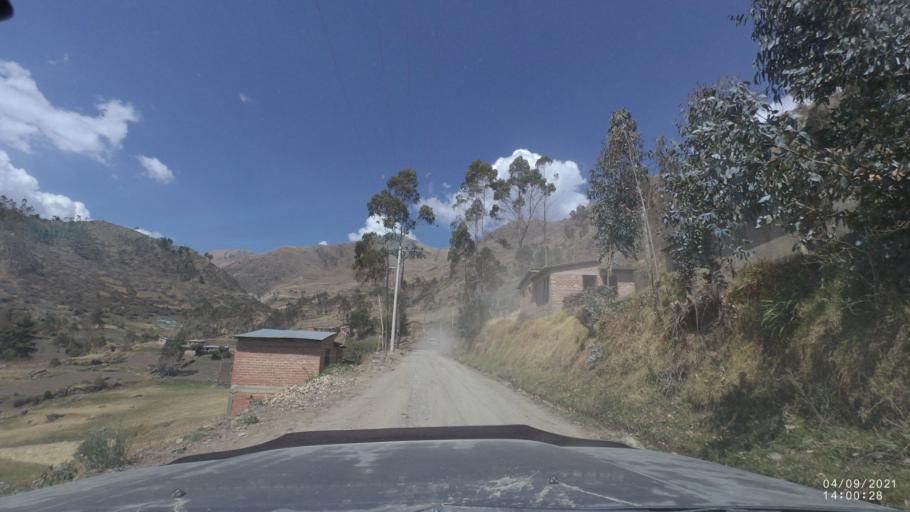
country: BO
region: Cochabamba
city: Sipe Sipe
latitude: -17.2318
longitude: -66.4847
